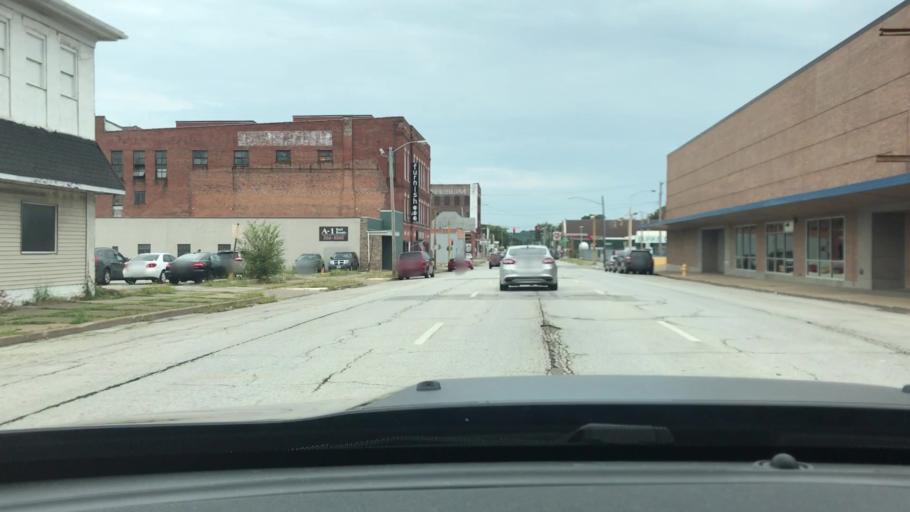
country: US
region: Iowa
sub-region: Scott County
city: Davenport
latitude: 41.5235
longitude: -90.5845
